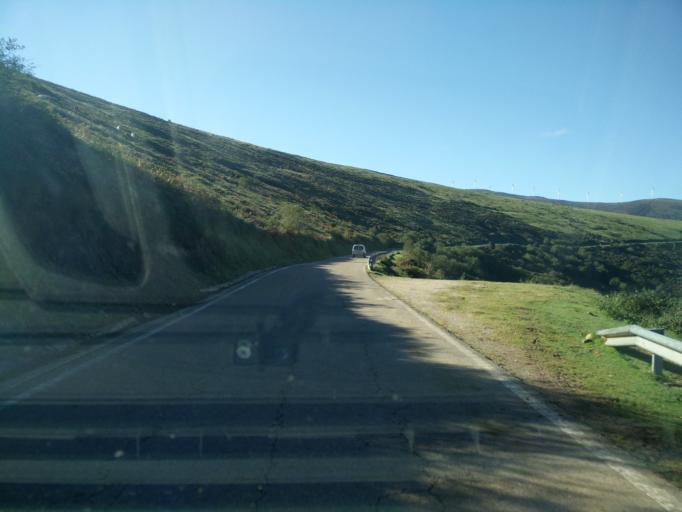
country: ES
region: Cantabria
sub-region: Provincia de Cantabria
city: San Pedro del Romeral
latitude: 43.0880
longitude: -3.8198
